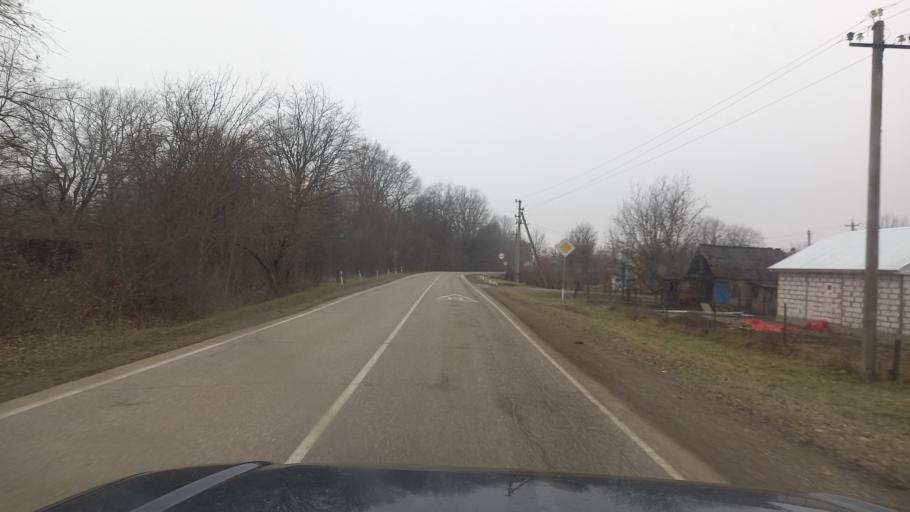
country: RU
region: Krasnodarskiy
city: Neftegorsk
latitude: 44.2923
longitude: 39.8252
